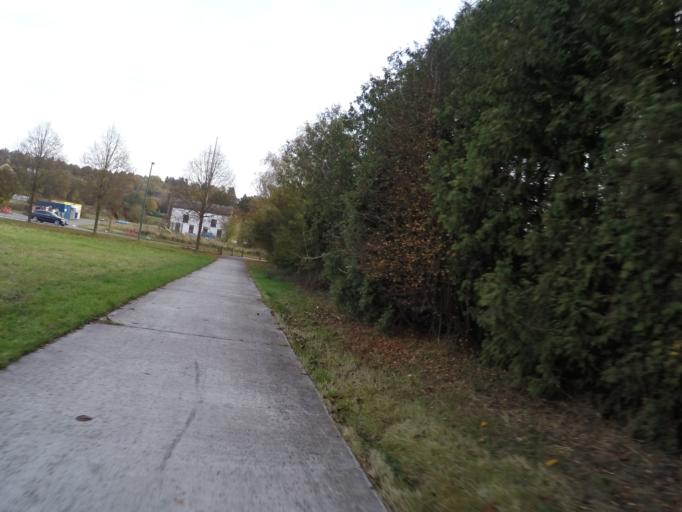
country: BE
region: Wallonia
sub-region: Province du Luxembourg
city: Marche-en-Famenne
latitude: 50.2341
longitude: 5.3550
